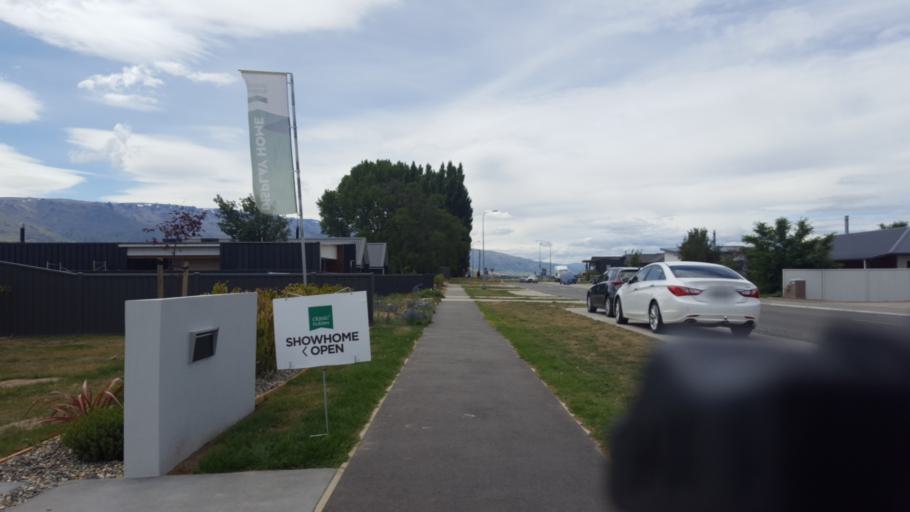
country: NZ
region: Otago
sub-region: Queenstown-Lakes District
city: Wanaka
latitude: -45.0387
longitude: 169.2157
